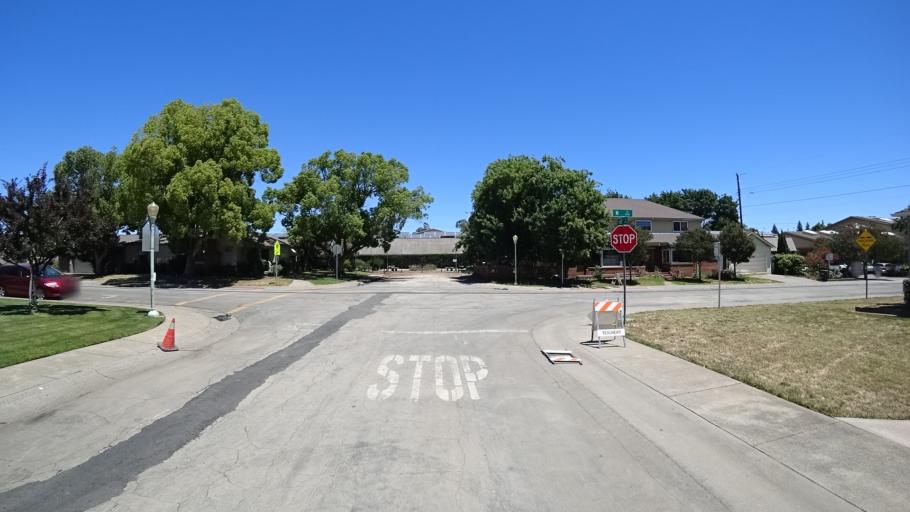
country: US
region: California
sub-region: Sacramento County
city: Florin
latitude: 38.5588
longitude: -121.4313
